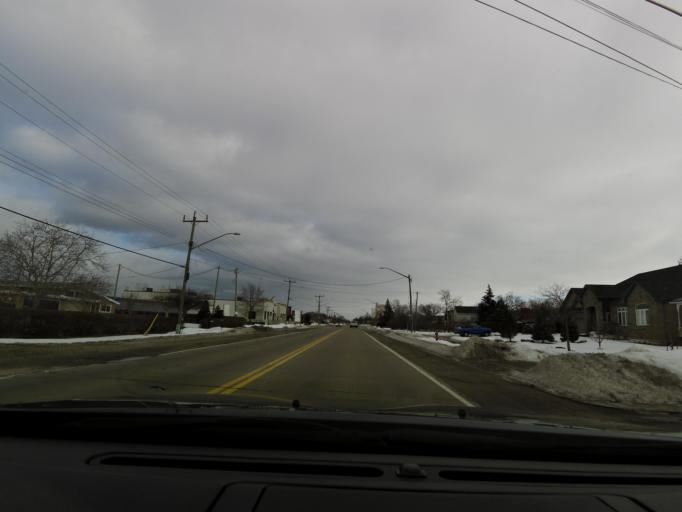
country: CA
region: Ontario
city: Hamilton
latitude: 43.2087
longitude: -79.6566
